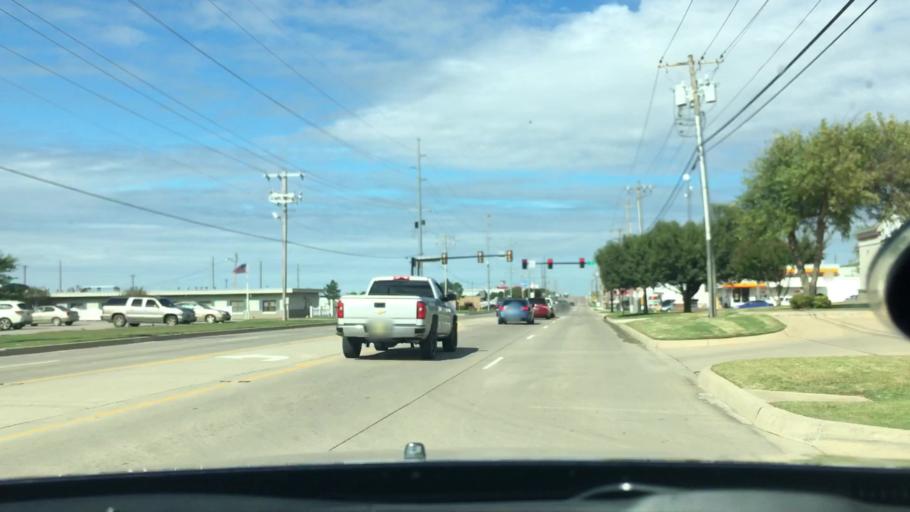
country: US
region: Oklahoma
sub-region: Pontotoc County
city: Ada
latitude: 34.7844
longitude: -96.6523
